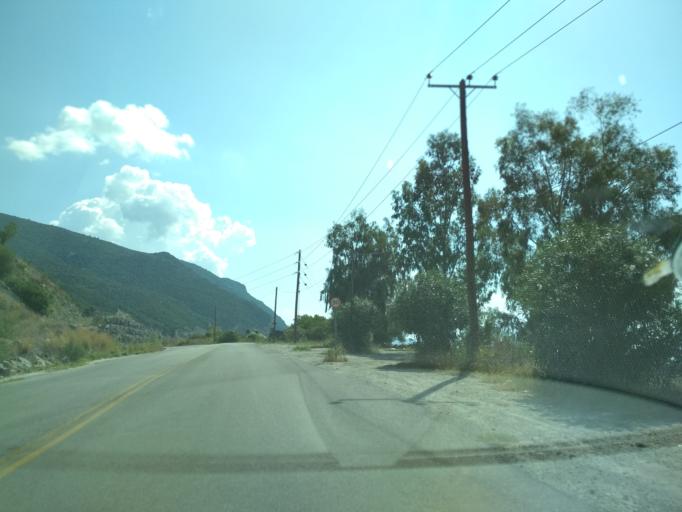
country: GR
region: Central Greece
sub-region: Nomos Evvoias
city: Oreoi
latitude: 38.8526
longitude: 23.1307
